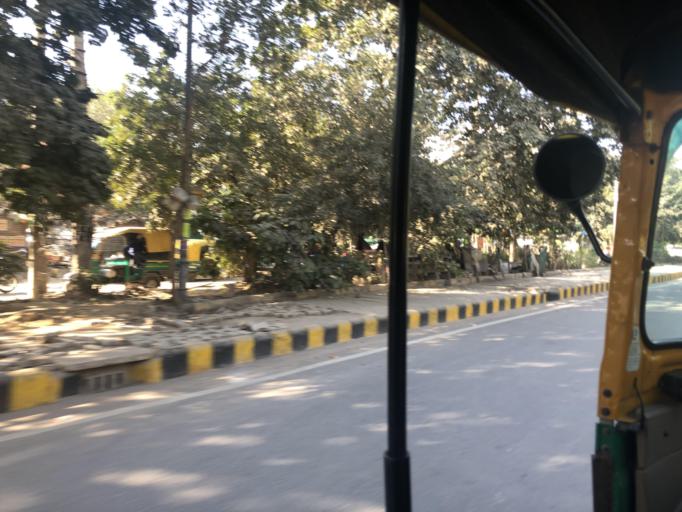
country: IN
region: Haryana
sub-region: Gurgaon
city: Gurgaon
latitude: 28.4502
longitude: 77.0694
